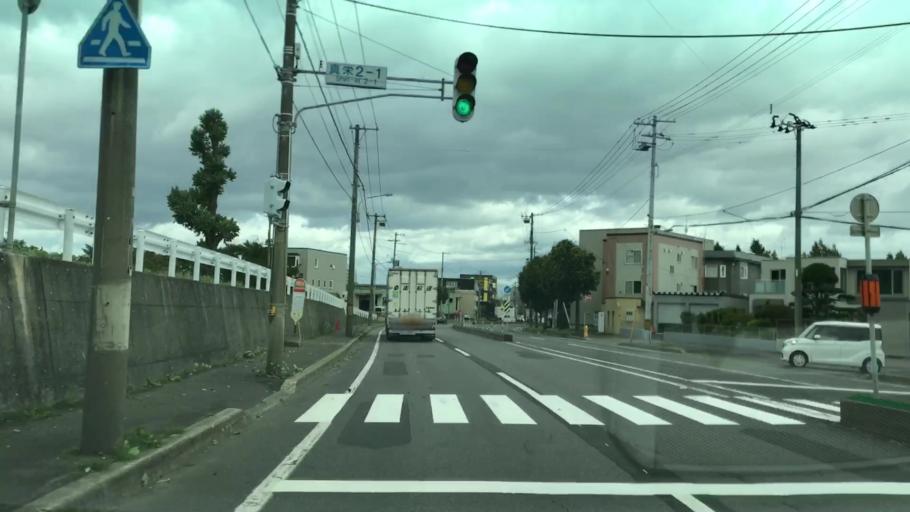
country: JP
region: Hokkaido
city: Sapporo
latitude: 42.9913
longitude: 141.4407
